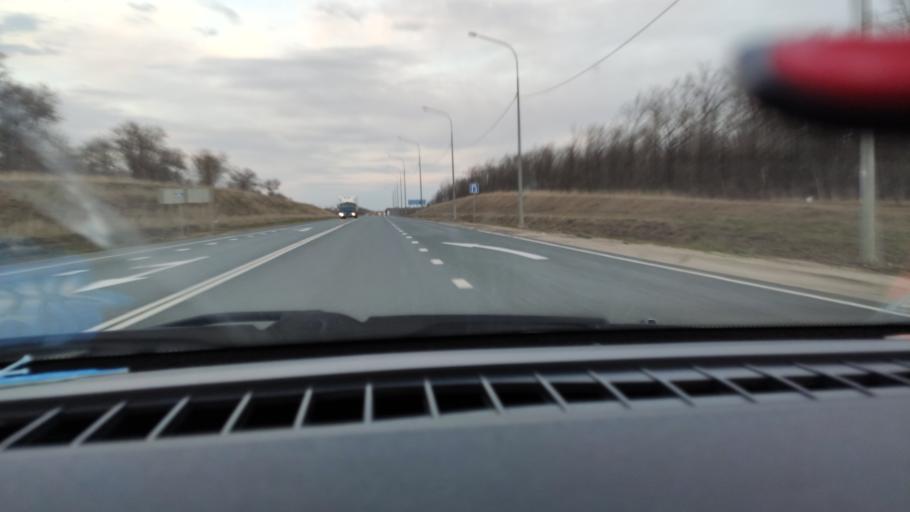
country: RU
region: Saratov
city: Yelshanka
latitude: 51.8227
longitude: 46.3213
